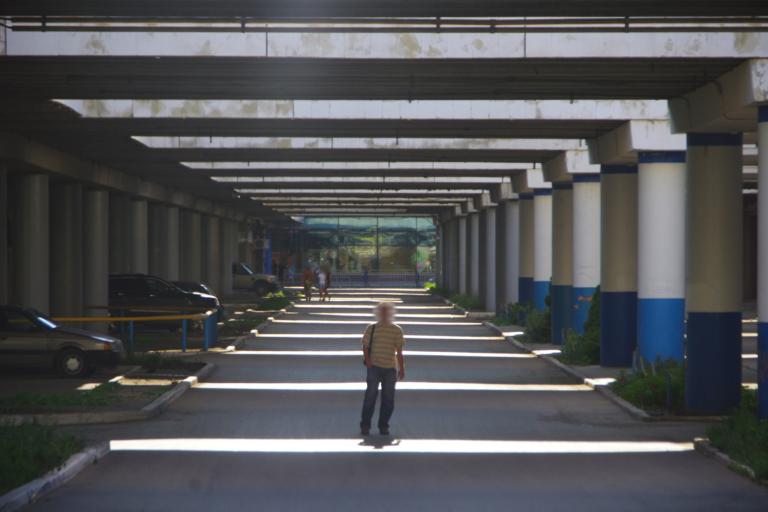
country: RU
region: Samara
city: Tol'yatti
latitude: 53.5175
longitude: 49.2774
